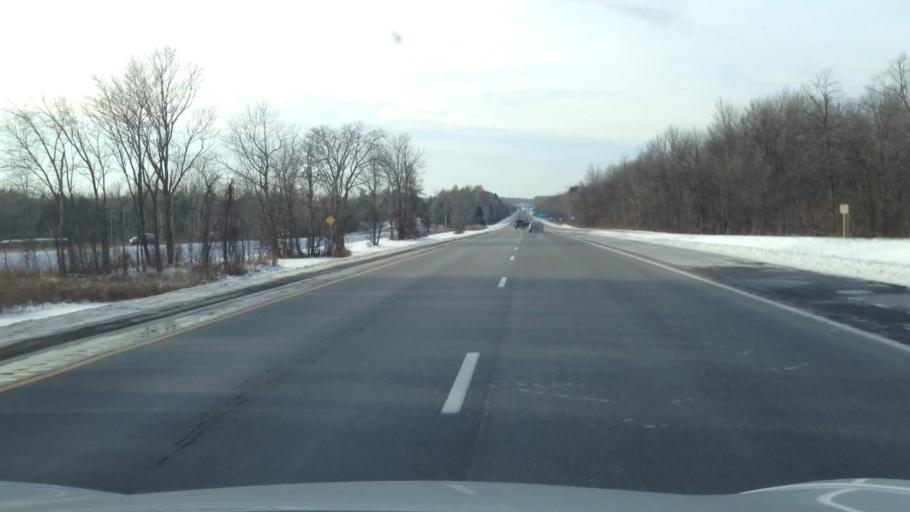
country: CA
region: Quebec
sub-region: Laurentides
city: Brownsburg-Chatham
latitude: 45.5483
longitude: -74.4253
